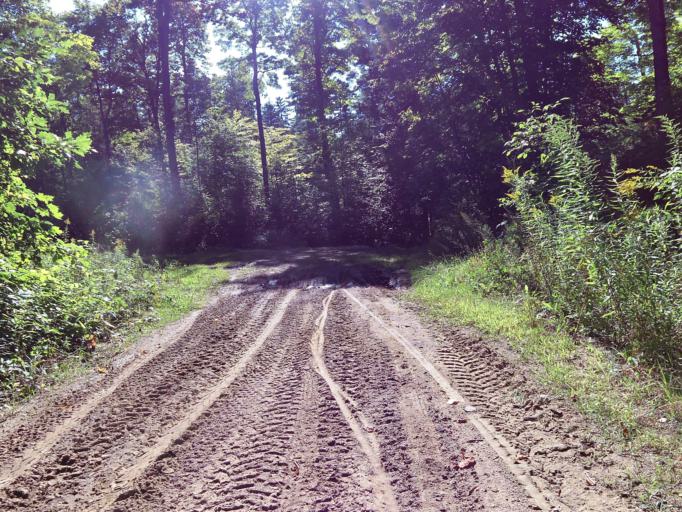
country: CA
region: Ontario
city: Renfrew
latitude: 45.1268
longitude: -76.7370
